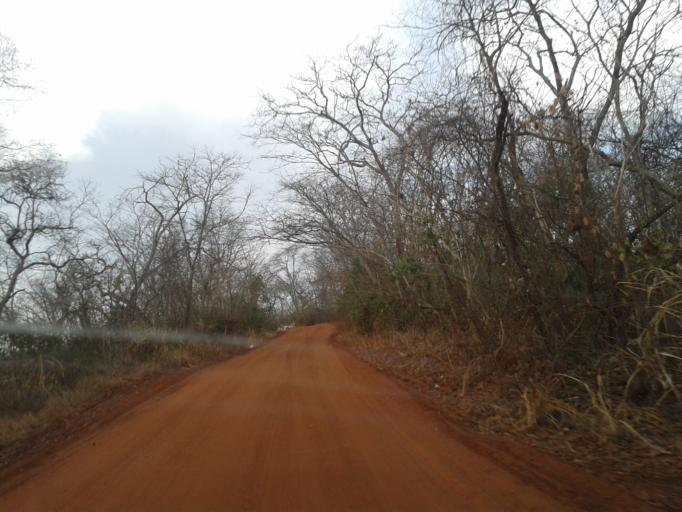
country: BR
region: Minas Gerais
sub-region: Santa Vitoria
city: Santa Vitoria
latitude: -19.1851
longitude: -49.8611
